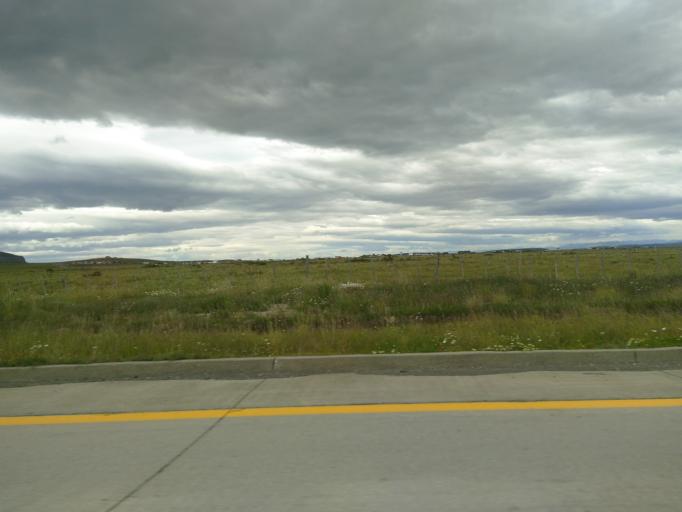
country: CL
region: Magallanes
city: Puerto Natales
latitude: -51.6821
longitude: -72.5221
